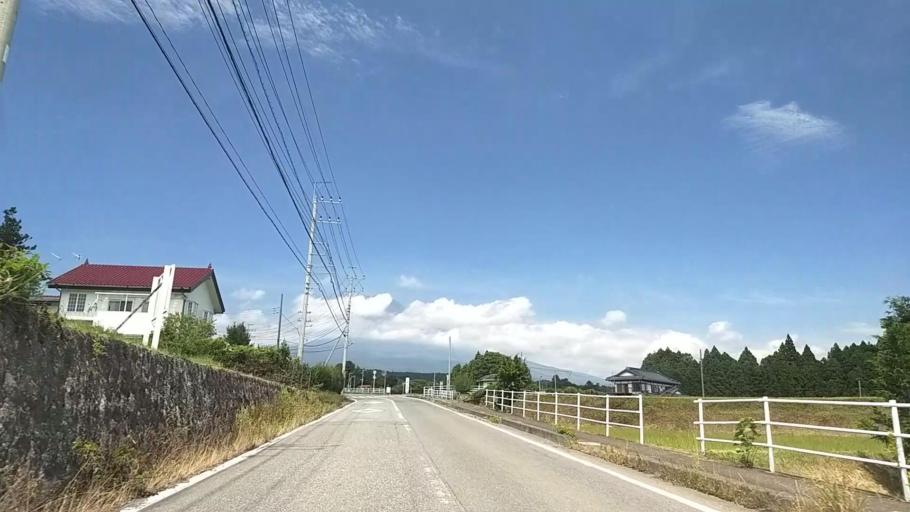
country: JP
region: Shizuoka
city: Gotemba
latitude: 35.2474
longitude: 138.8530
